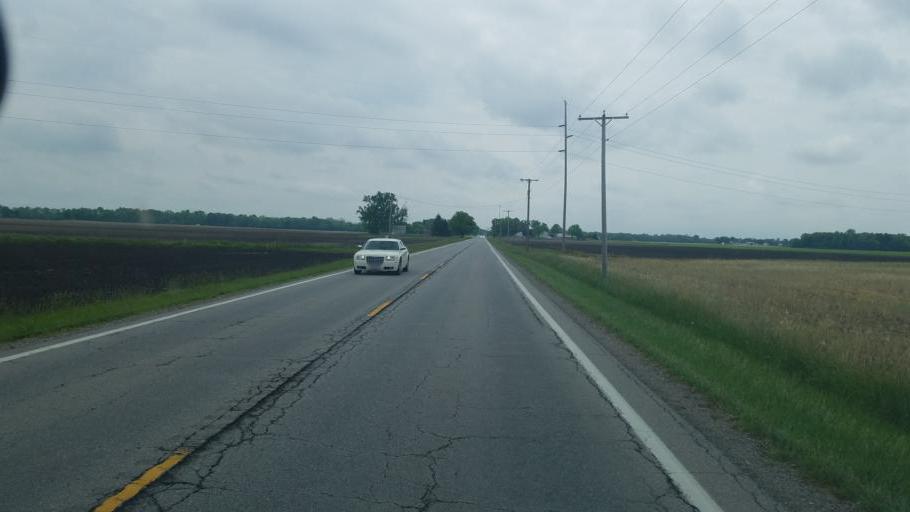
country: US
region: Ohio
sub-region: Union County
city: Richwood
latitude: 40.4068
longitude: -83.2595
